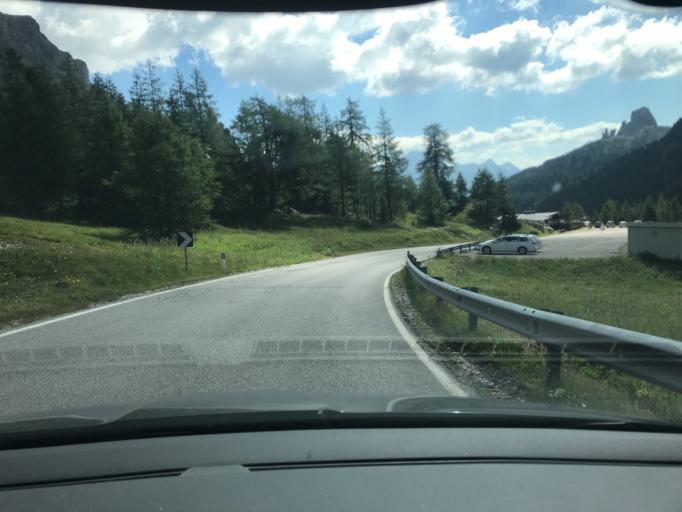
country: IT
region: Veneto
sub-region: Provincia di Belluno
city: Colle Santa Lucia
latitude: 46.5208
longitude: 12.0172
